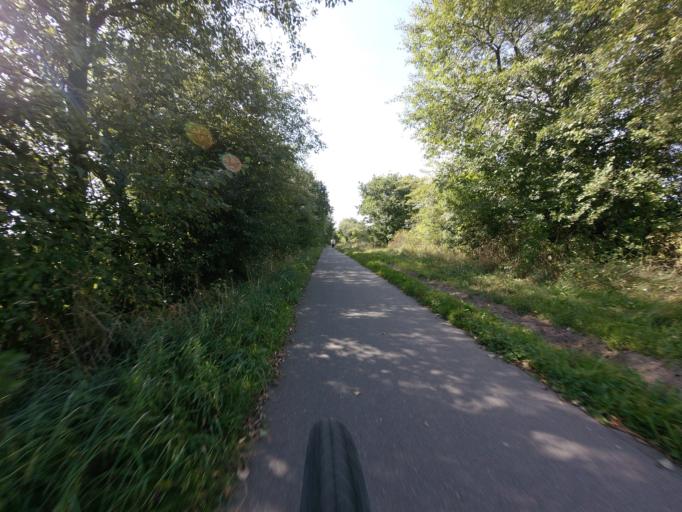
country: DK
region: Central Jutland
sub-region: Viborg Kommune
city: Viborg
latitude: 56.4206
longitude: 9.3790
